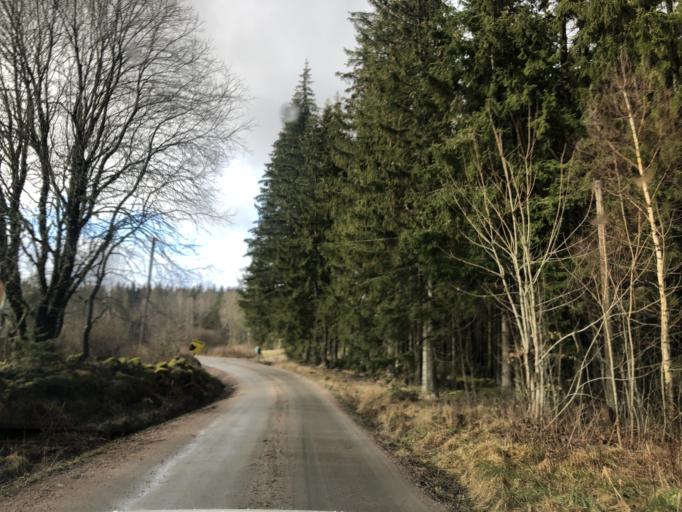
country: SE
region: Vaestra Goetaland
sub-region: Ulricehamns Kommun
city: Ulricehamn
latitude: 57.8282
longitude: 13.2377
